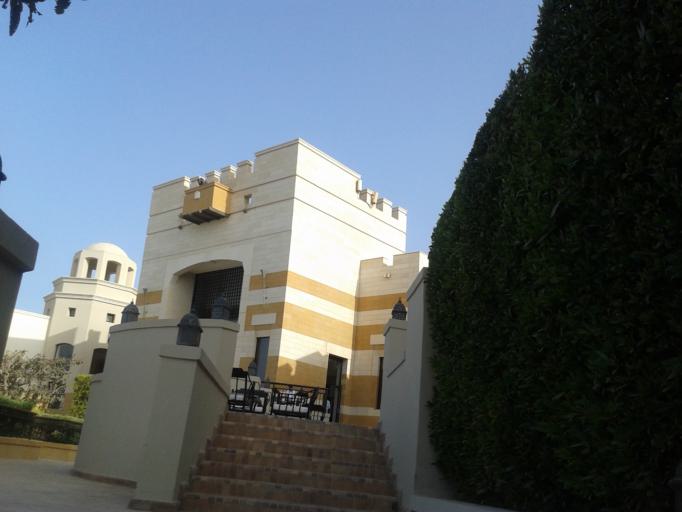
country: EG
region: Red Sea
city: Marsa Alam
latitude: 25.5360
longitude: 34.6390
